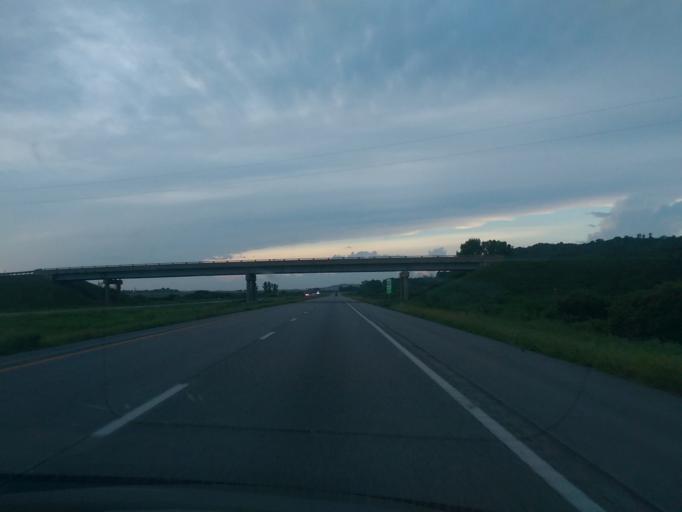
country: US
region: Missouri
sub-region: Atchison County
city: Rock Port
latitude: 40.3000
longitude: -95.4881
